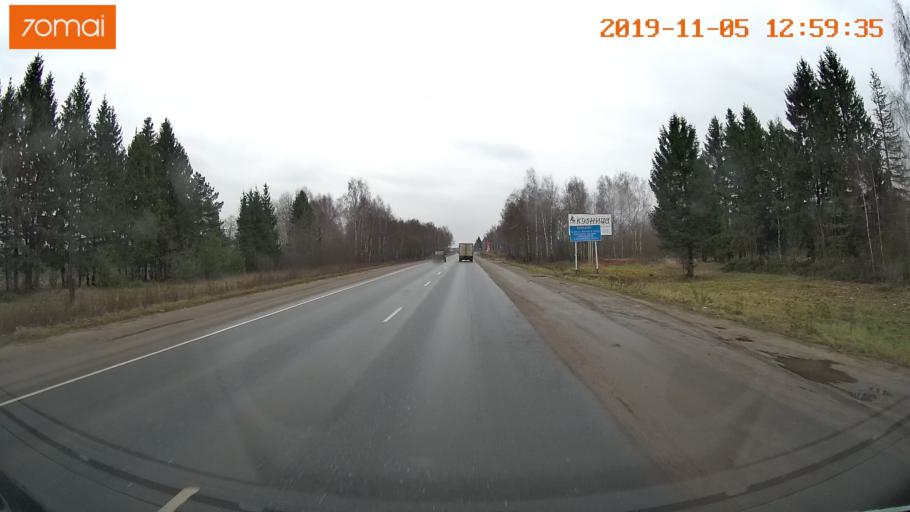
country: RU
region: Ivanovo
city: Kokhma
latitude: 56.9177
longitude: 41.1317
